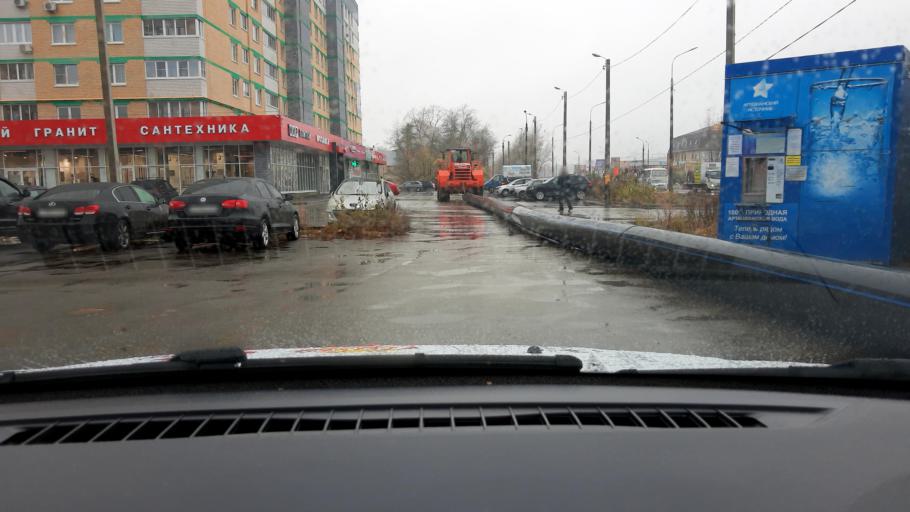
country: RU
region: Nizjnij Novgorod
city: Dzerzhinsk
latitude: 56.2464
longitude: 43.4127
